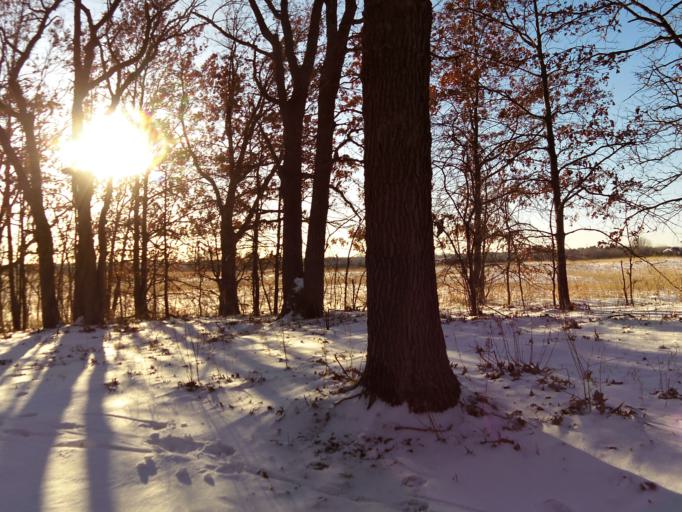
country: US
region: Minnesota
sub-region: Washington County
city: Lake Elmo
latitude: 44.9881
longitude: -92.9134
